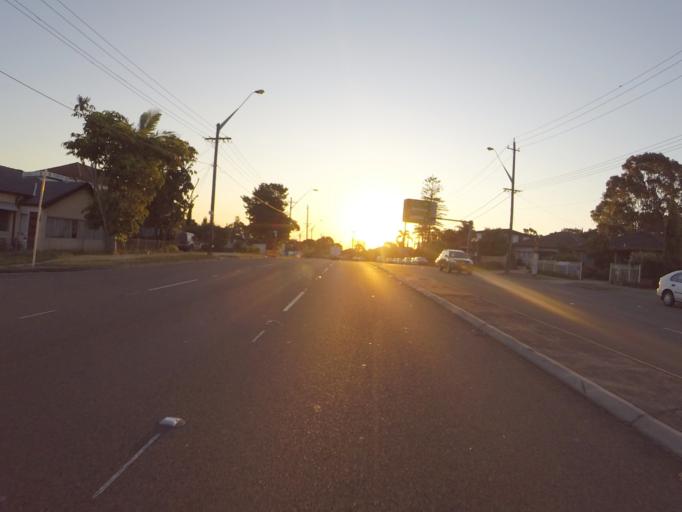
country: AU
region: New South Wales
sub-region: Hurstville
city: Peakhurst
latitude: -33.9578
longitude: 151.0672
